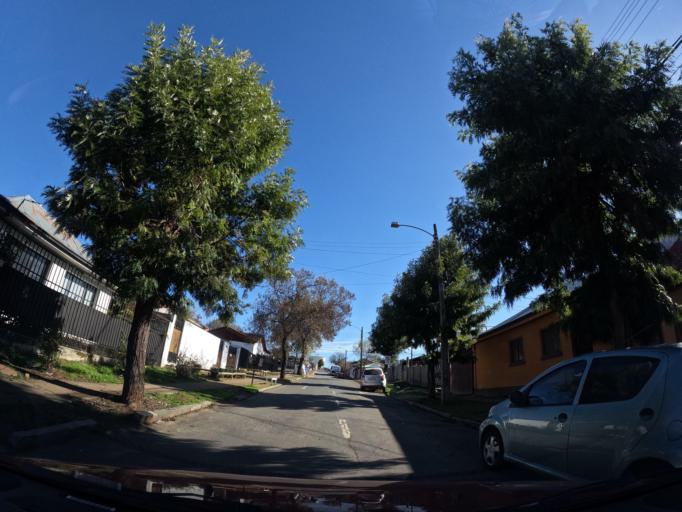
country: CL
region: Maule
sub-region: Provincia de Cauquenes
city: Cauquenes
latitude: -35.9712
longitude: -72.3172
